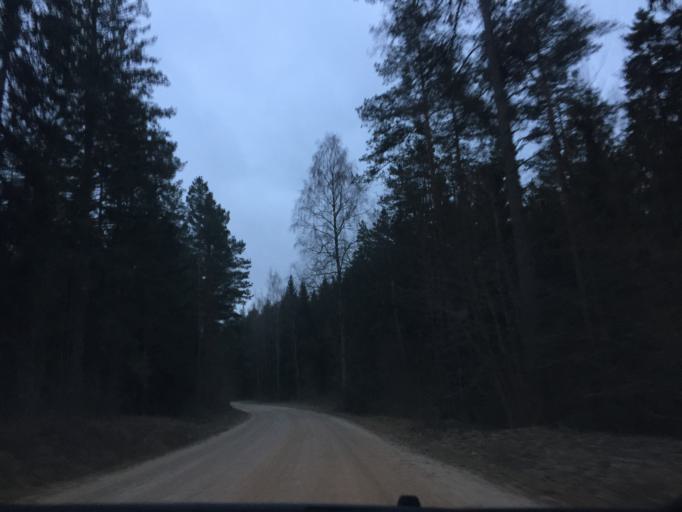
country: LV
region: Cesu Rajons
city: Cesis
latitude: 57.3439
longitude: 25.2585
